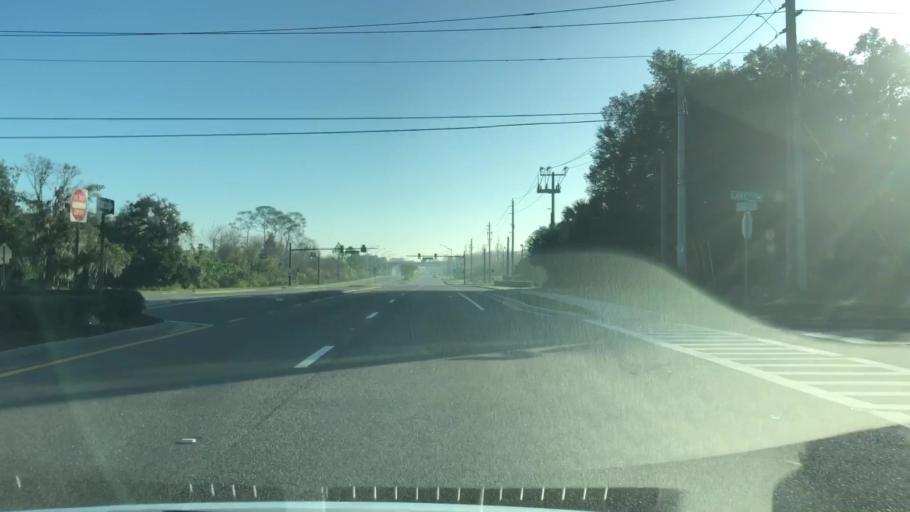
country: US
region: Florida
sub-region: Seminole County
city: Lake Mary
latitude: 28.7864
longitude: -81.3072
